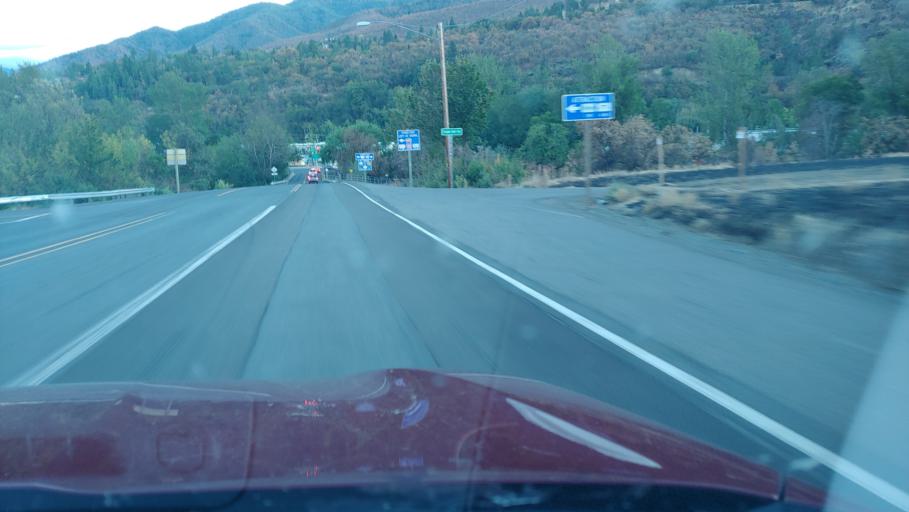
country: US
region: Oregon
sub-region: Jackson County
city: Ashland
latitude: 42.2233
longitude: -122.7406
